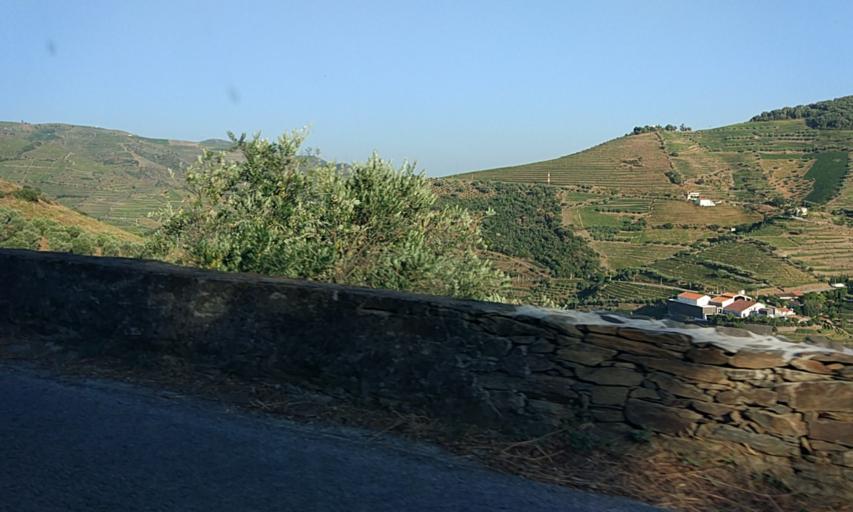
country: PT
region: Viseu
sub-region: Tabuaco
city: Tabuaco
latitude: 41.1652
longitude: -7.5281
